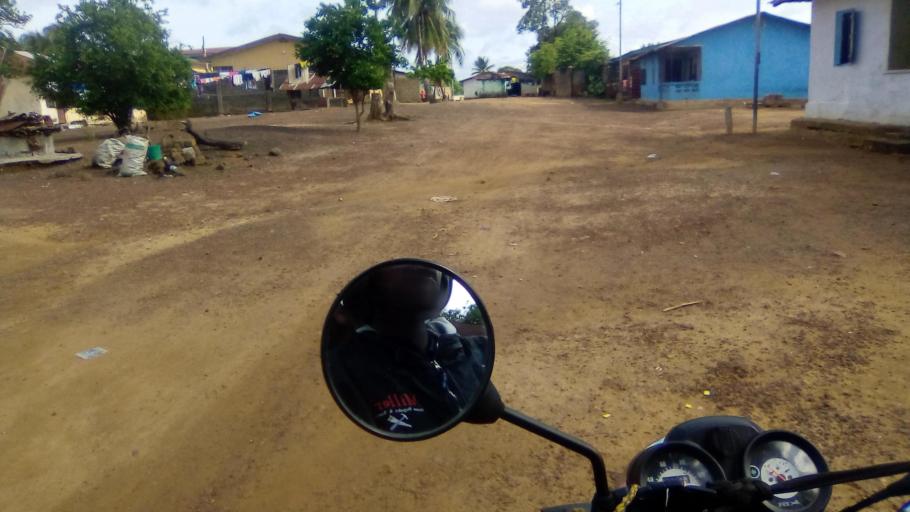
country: SL
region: Southern Province
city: Bo
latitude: 7.9584
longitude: -11.7565
